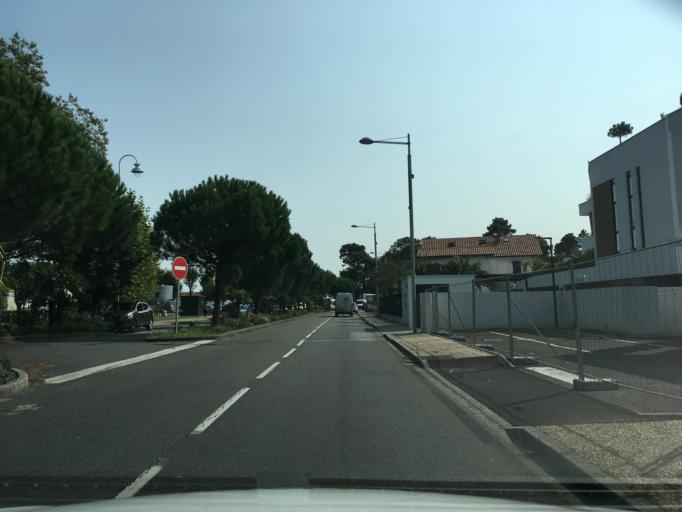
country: FR
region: Aquitaine
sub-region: Departement des Pyrenees-Atlantiques
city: Bayonne
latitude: 43.5130
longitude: -1.5002
